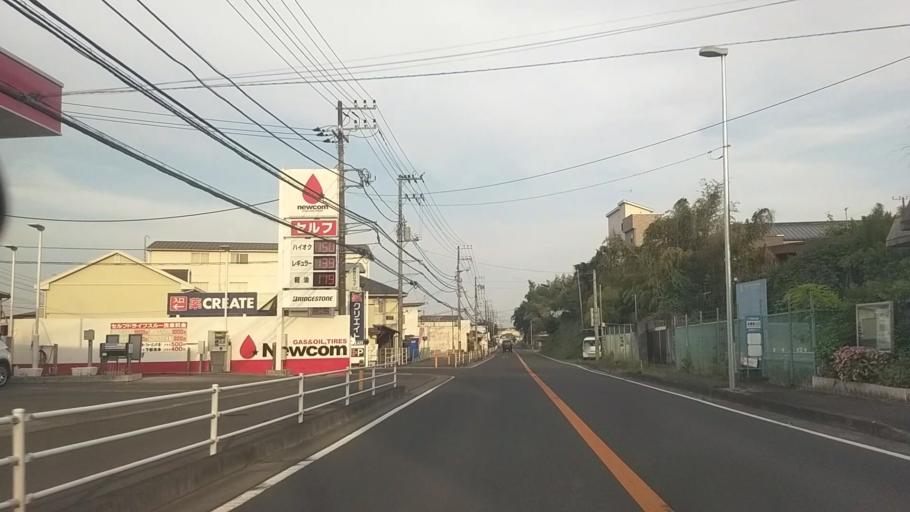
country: JP
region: Kanagawa
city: Odawara
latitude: 35.2827
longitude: 139.1442
